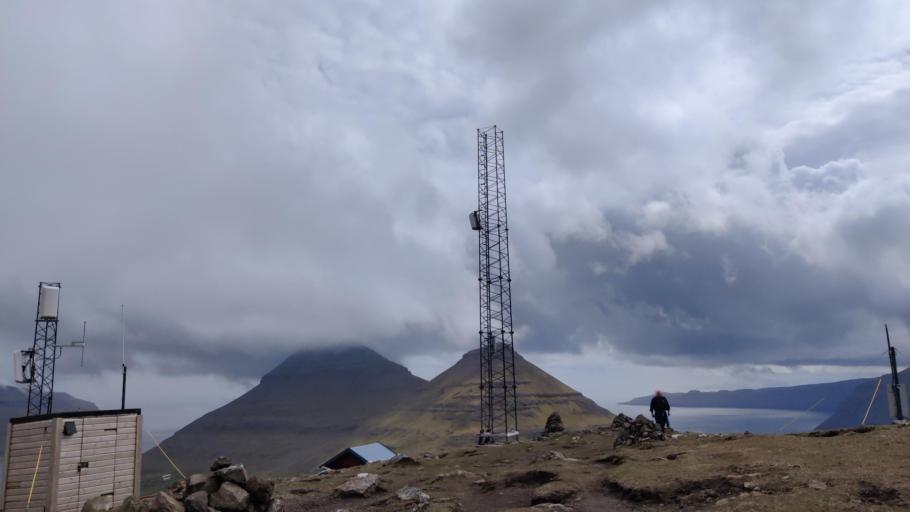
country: FO
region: Nordoyar
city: Klaksvik
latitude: 62.2350
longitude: -6.6166
